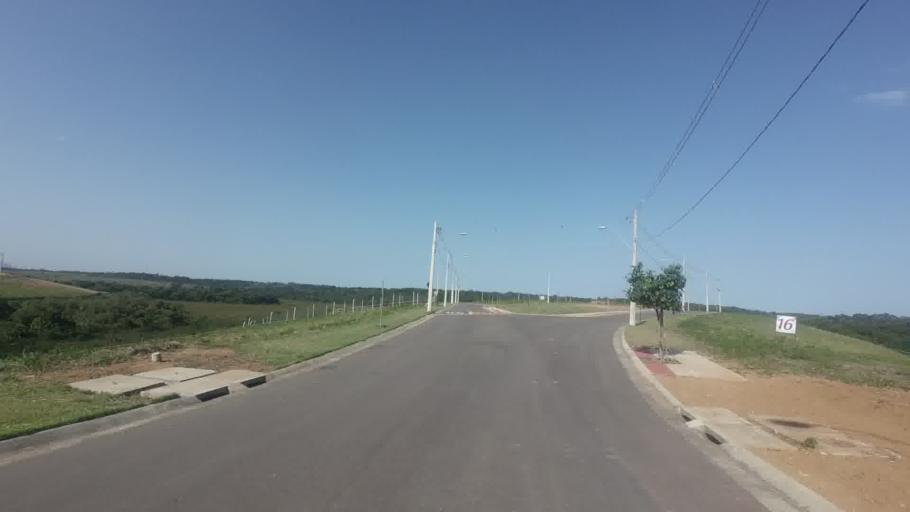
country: BR
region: Espirito Santo
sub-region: Guarapari
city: Guarapari
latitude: -20.7138
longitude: -40.5312
